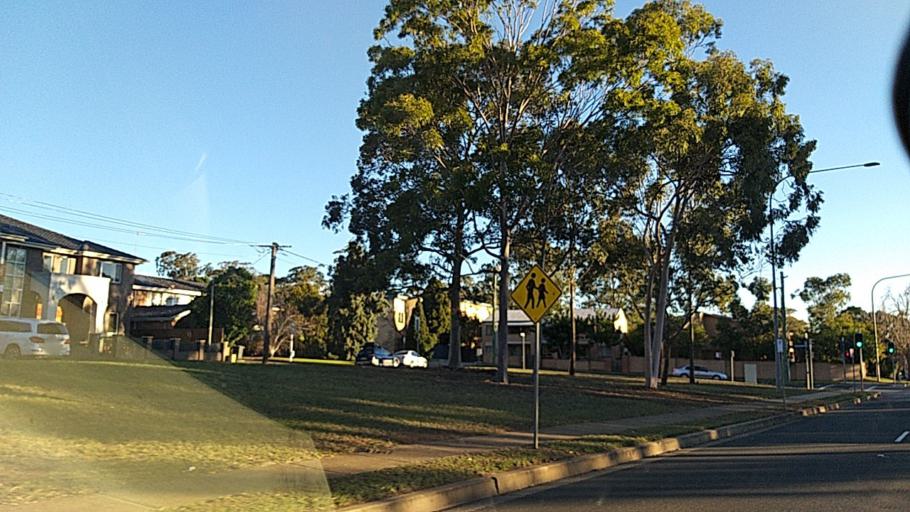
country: AU
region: New South Wales
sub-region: Campbelltown Municipality
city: Campbelltown
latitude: -34.0676
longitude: 150.8178
